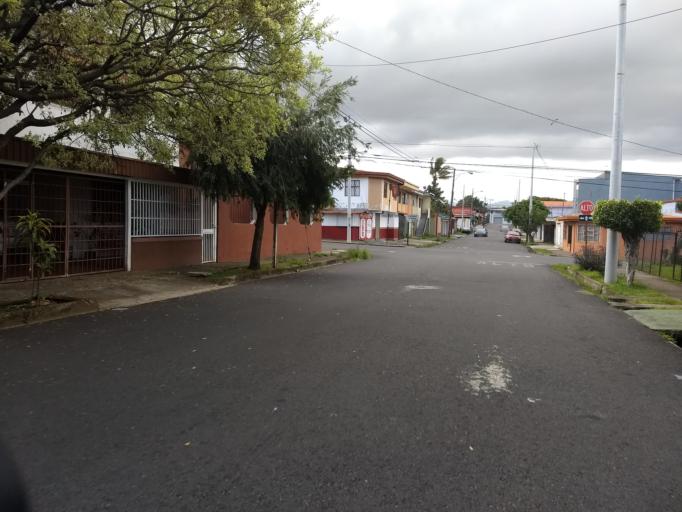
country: CR
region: San Jose
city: San Juan
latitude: 9.9593
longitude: -84.0828
